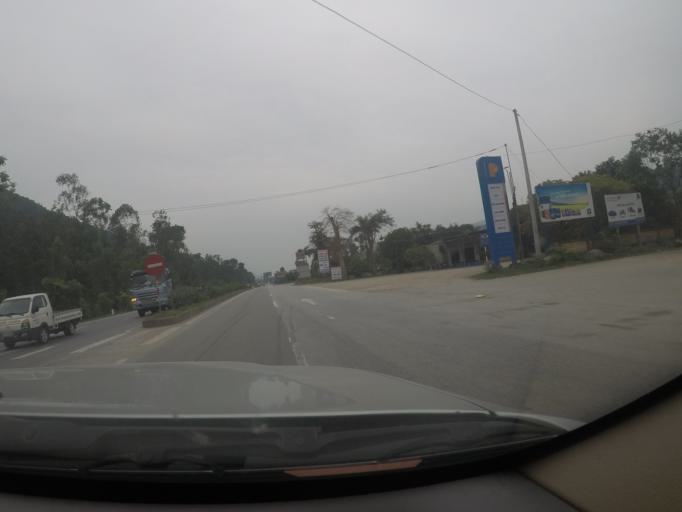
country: VN
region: Nghe An
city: Dien Chau
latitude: 18.8793
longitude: 105.6098
